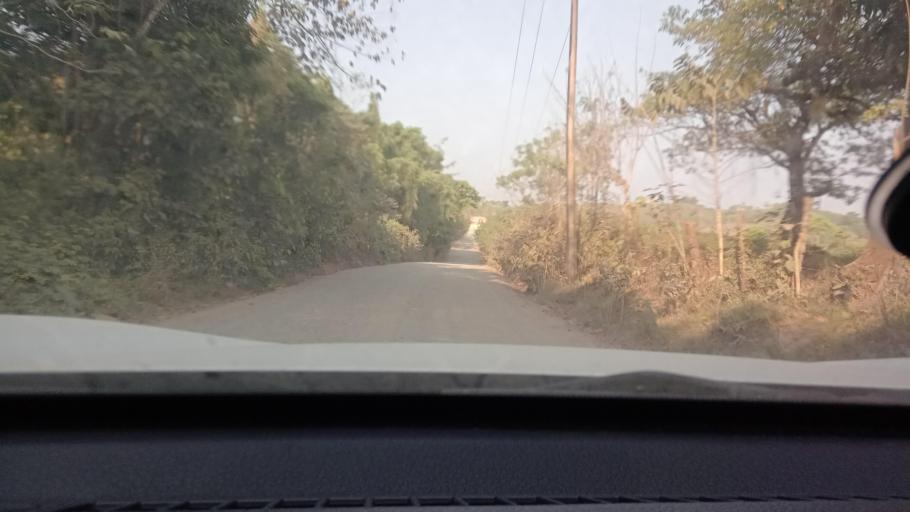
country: MX
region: Tabasco
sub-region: Huimanguillo
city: Francisco Rueda
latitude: 17.6575
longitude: -93.8667
